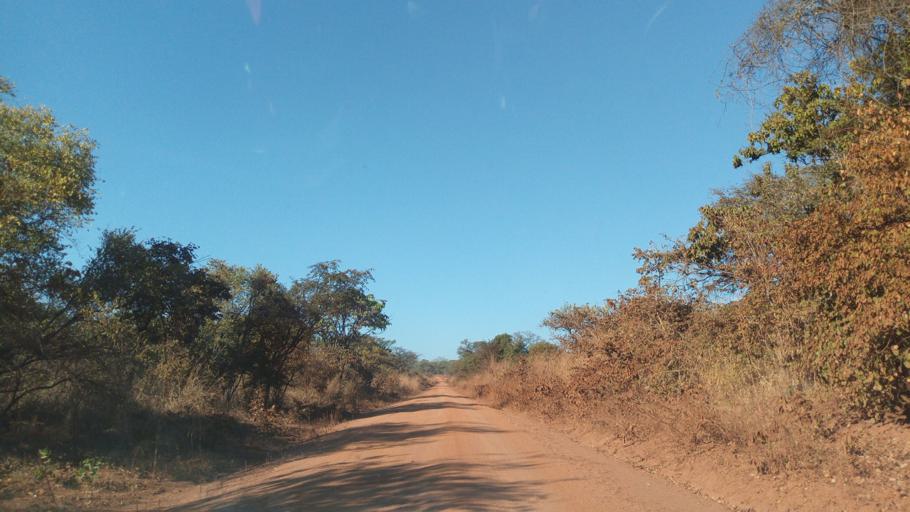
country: ZM
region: Luapula
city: Mwense
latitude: -10.5735
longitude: 28.4344
